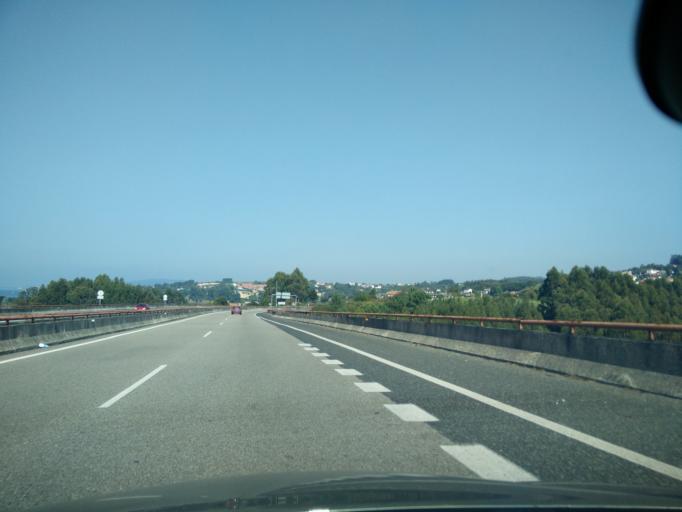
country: ES
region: Galicia
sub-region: Provincia da Coruna
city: Mino
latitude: 43.3523
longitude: -8.2014
